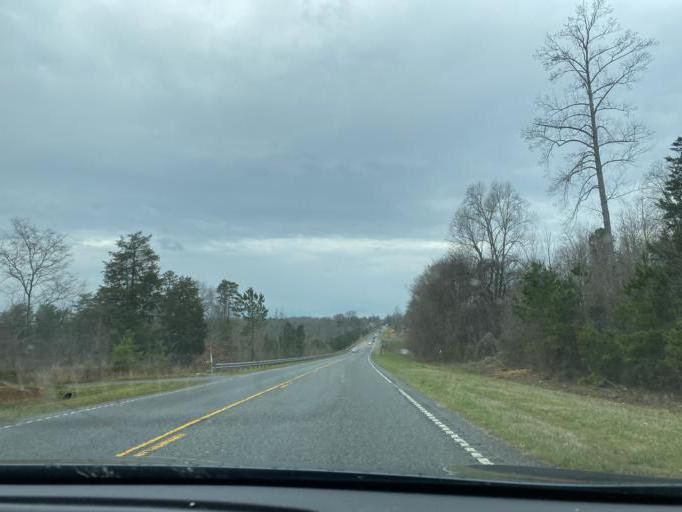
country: US
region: South Carolina
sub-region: Cherokee County
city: Gaffney
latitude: 35.0245
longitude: -81.7133
